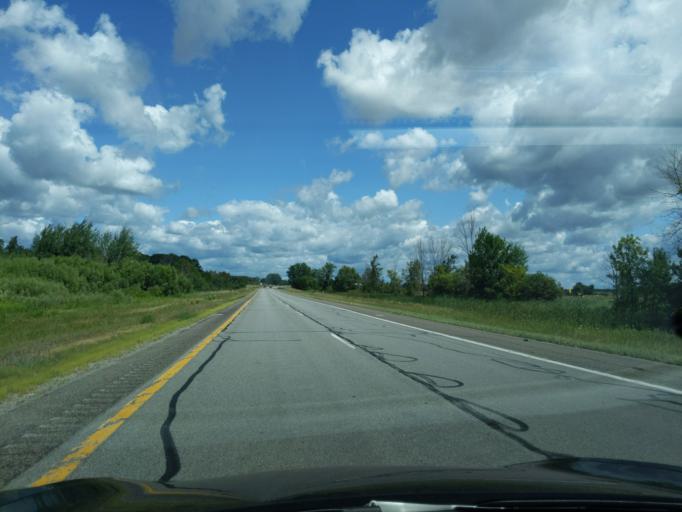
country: US
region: Michigan
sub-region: Clare County
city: Clare
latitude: 43.7573
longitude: -84.7576
